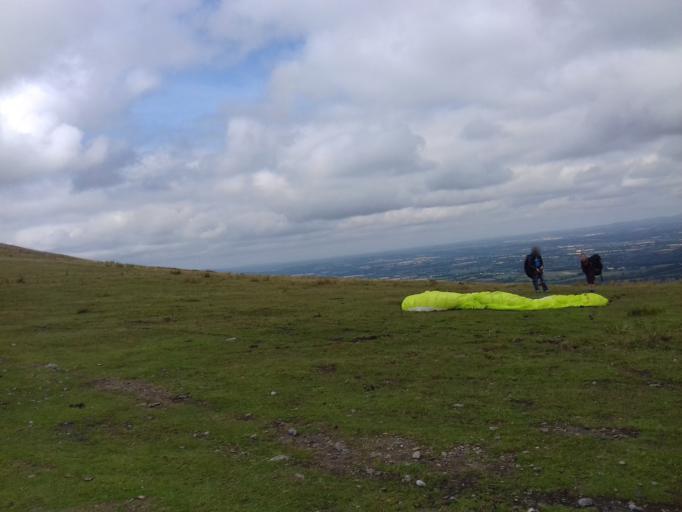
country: IE
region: Leinster
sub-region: Loch Garman
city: Bunclody
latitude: 52.6371
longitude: -6.7943
